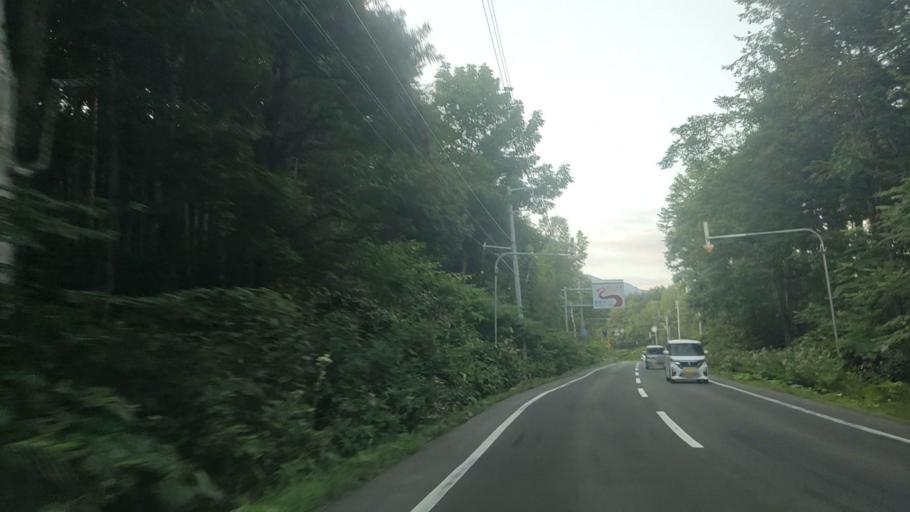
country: JP
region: Hokkaido
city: Bibai
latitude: 43.2554
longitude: 142.0267
